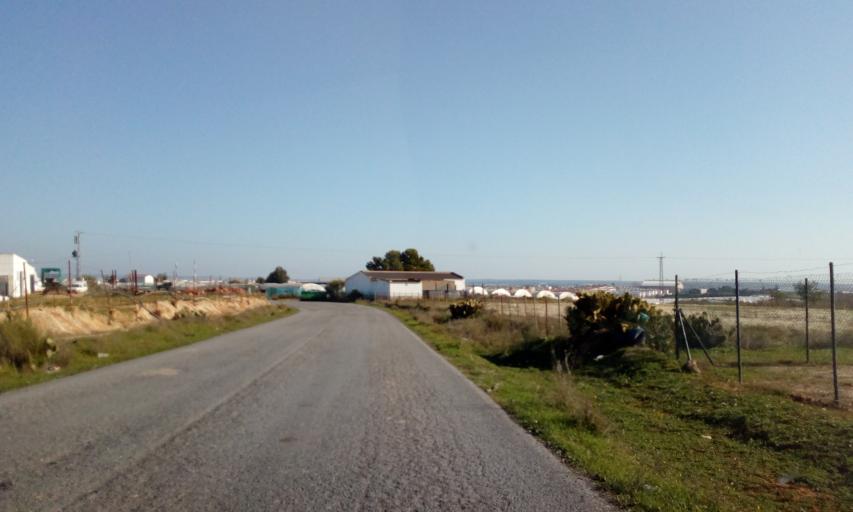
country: ES
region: Andalusia
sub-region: Provincia de Huelva
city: Lepe
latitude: 37.2452
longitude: -7.2202
